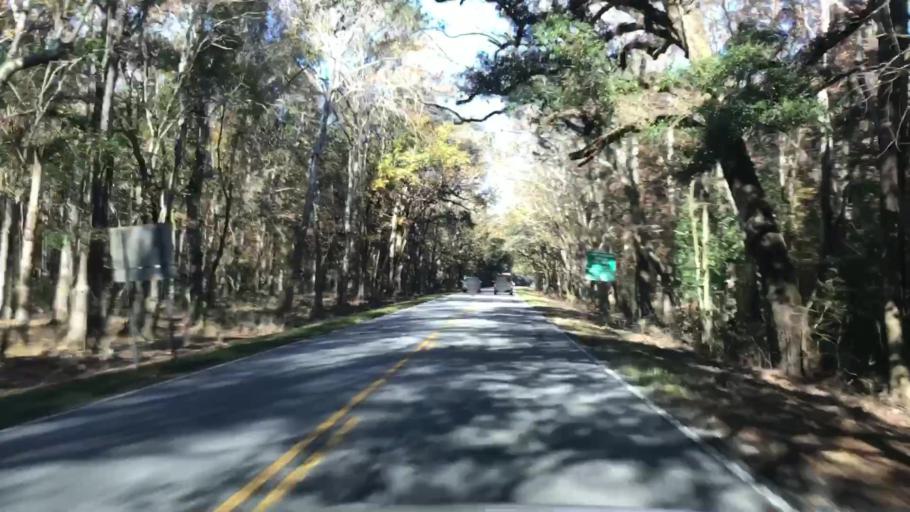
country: US
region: South Carolina
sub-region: Berkeley County
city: Ladson
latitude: 32.9112
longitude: -80.1508
